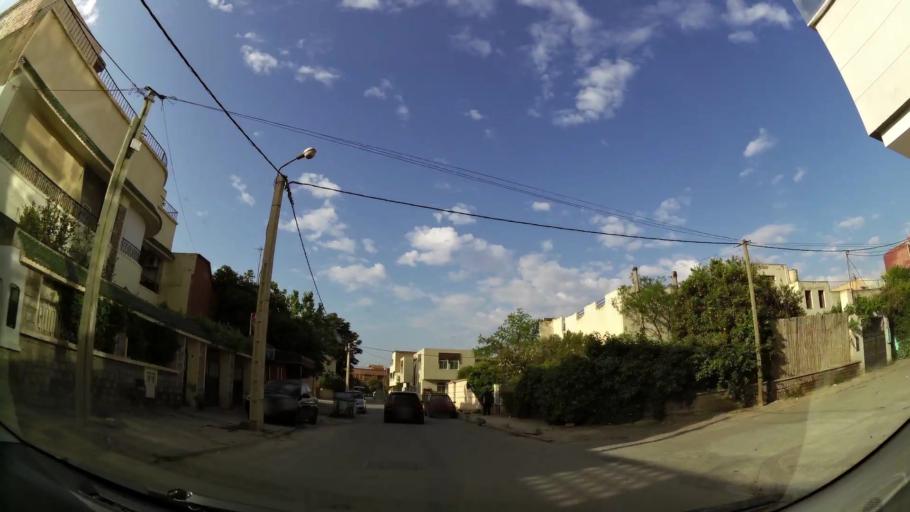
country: MA
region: Oriental
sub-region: Oujda-Angad
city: Oujda
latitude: 34.6728
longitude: -1.9255
